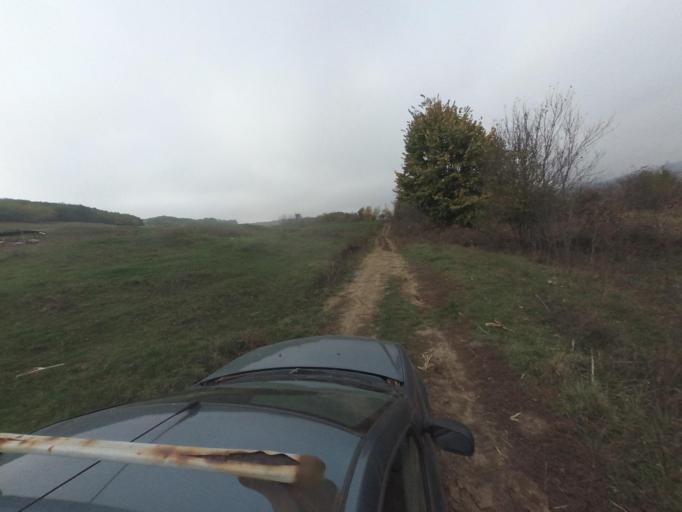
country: RO
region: Vaslui
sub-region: Comuna Bacesti
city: Bacesti
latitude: 46.8317
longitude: 27.2327
